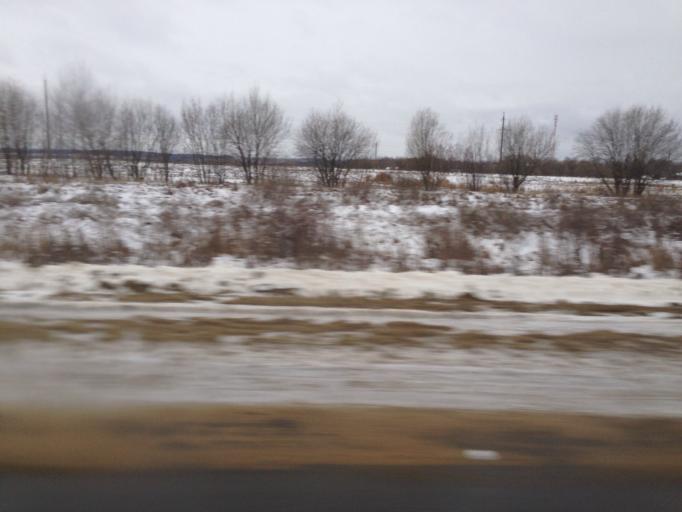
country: RU
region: Tula
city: Bolokhovo
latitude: 54.0543
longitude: 37.8090
